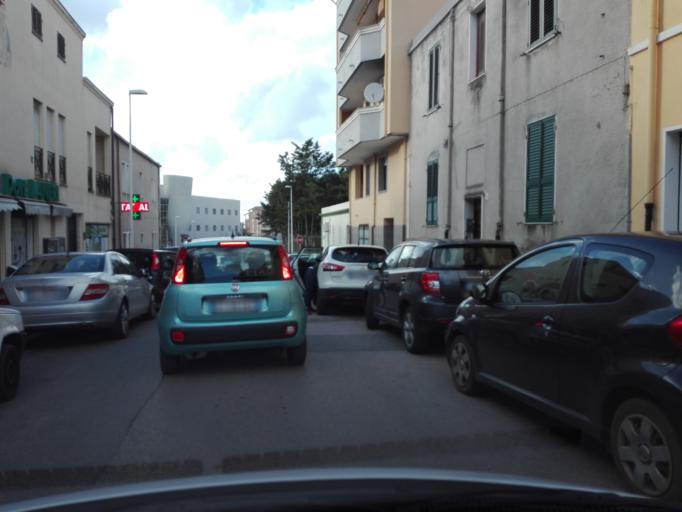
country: IT
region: Sardinia
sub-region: Provincia di Sassari
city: Sassari
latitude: 40.7350
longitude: 8.5648
